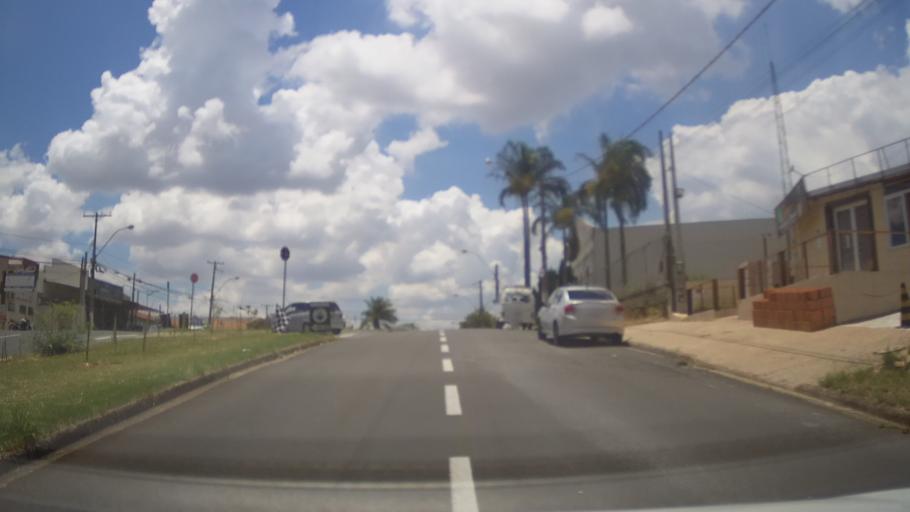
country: BR
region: Sao Paulo
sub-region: Valinhos
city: Valinhos
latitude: -22.9836
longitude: -46.9971
